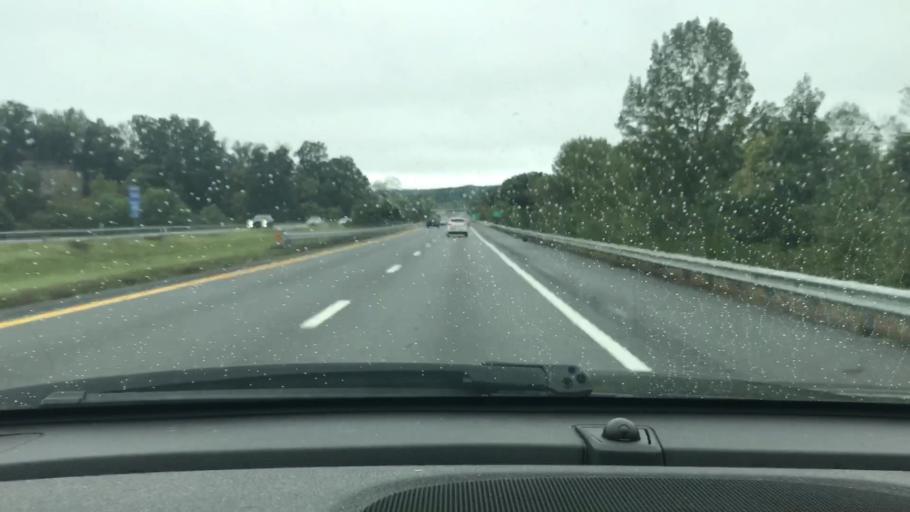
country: US
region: Tennessee
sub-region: Cheatham County
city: Kingston Springs
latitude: 36.0856
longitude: -87.0868
